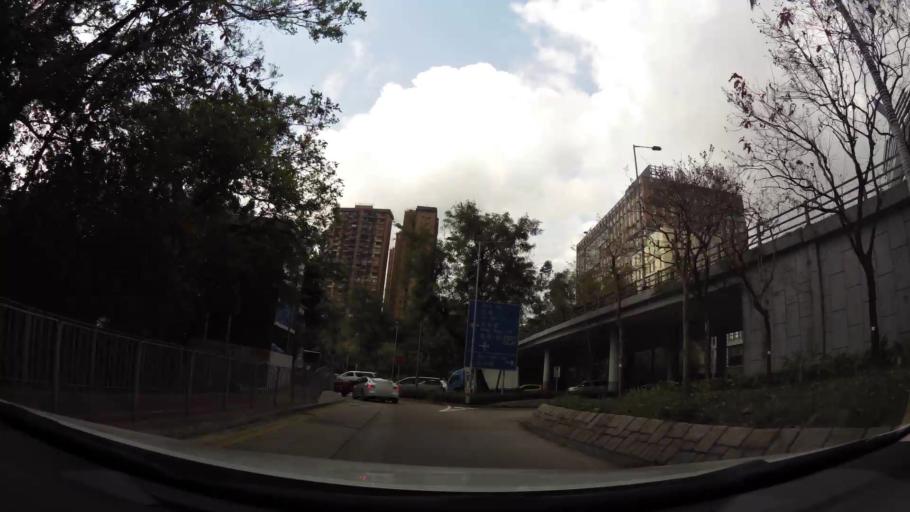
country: HK
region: Kowloon City
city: Kowloon
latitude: 22.3055
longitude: 114.1783
